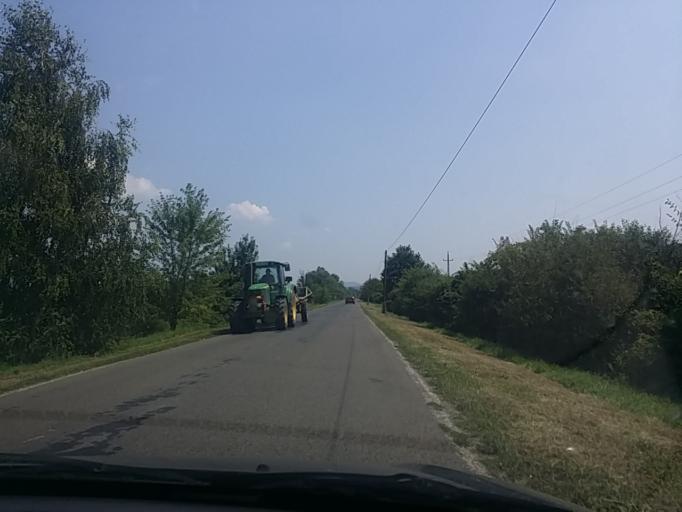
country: HU
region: Baranya
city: Sasd
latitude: 46.1941
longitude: 18.1335
